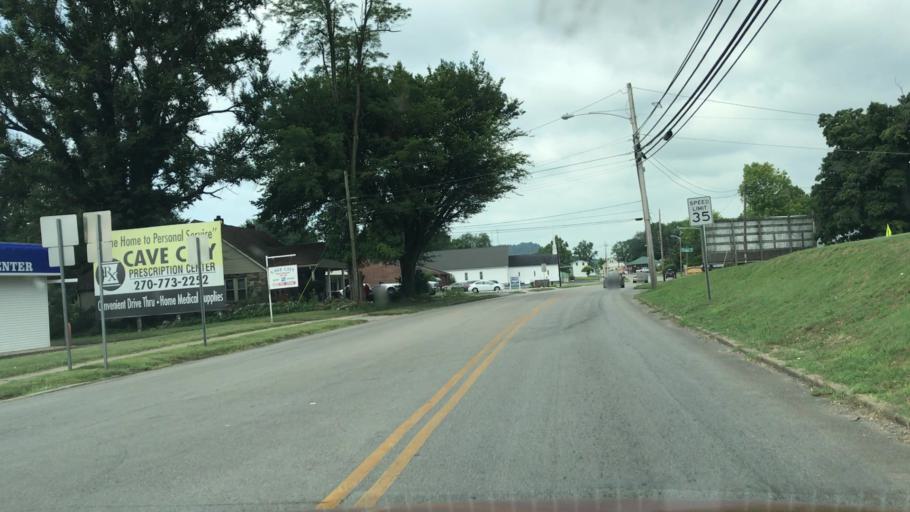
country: US
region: Kentucky
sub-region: Barren County
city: Cave City
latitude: 37.1353
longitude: -85.9564
